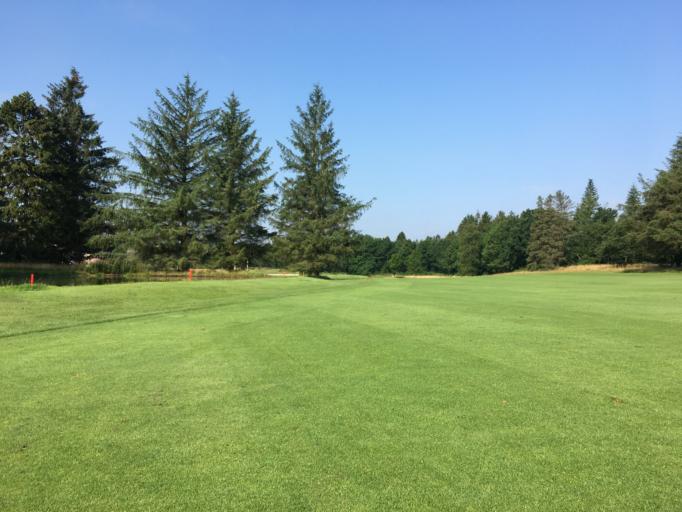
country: DK
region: Central Jutland
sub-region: Holstebro Kommune
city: Ulfborg
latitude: 56.3222
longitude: 8.4306
